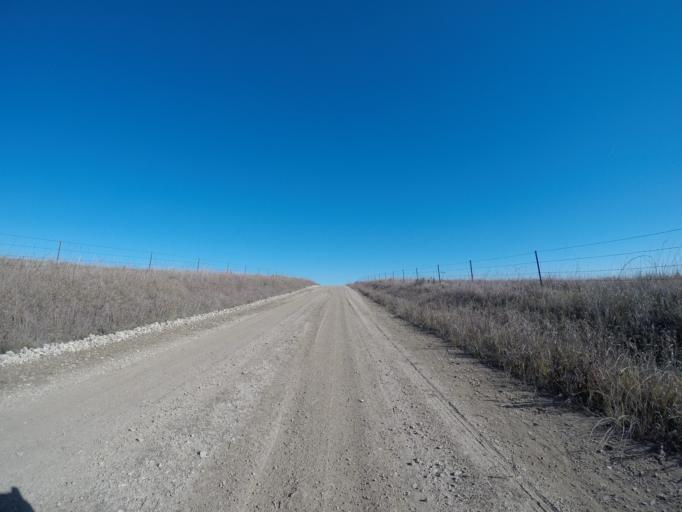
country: US
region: Kansas
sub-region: Wabaunsee County
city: Alma
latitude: 38.8869
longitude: -96.4008
